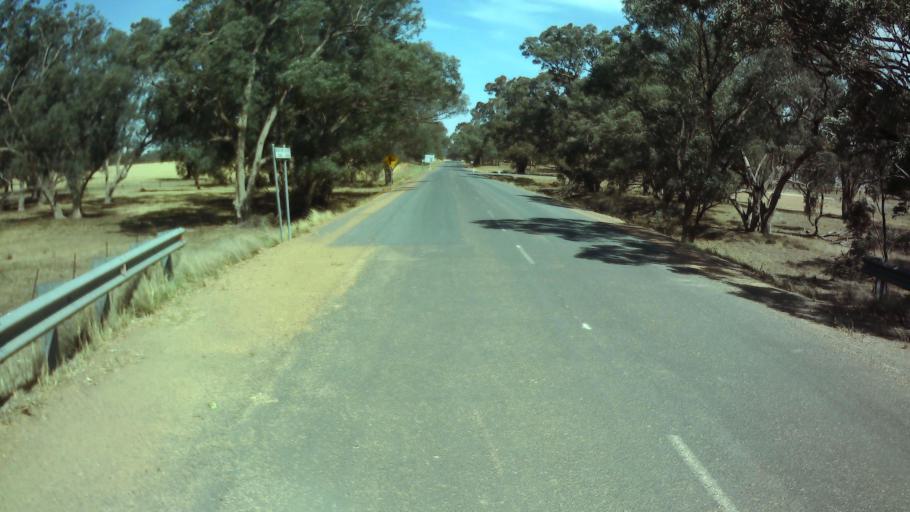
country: AU
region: New South Wales
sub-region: Weddin
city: Grenfell
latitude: -34.0807
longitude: 148.1474
